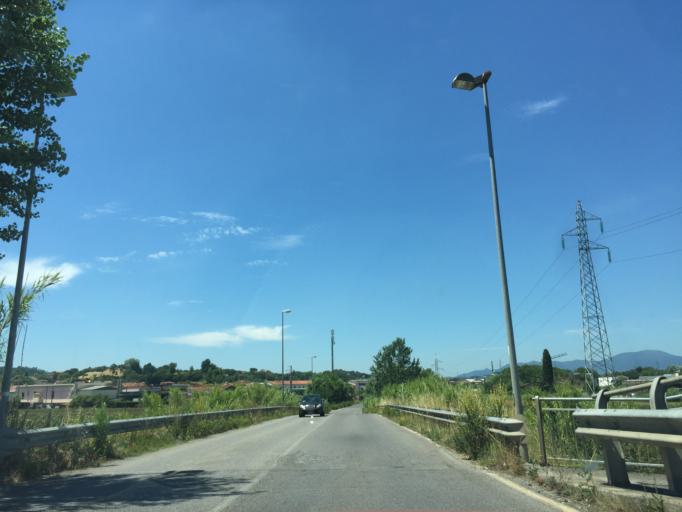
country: IT
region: Tuscany
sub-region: Province of Pisa
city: San Miniato
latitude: 43.6903
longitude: 10.7991
